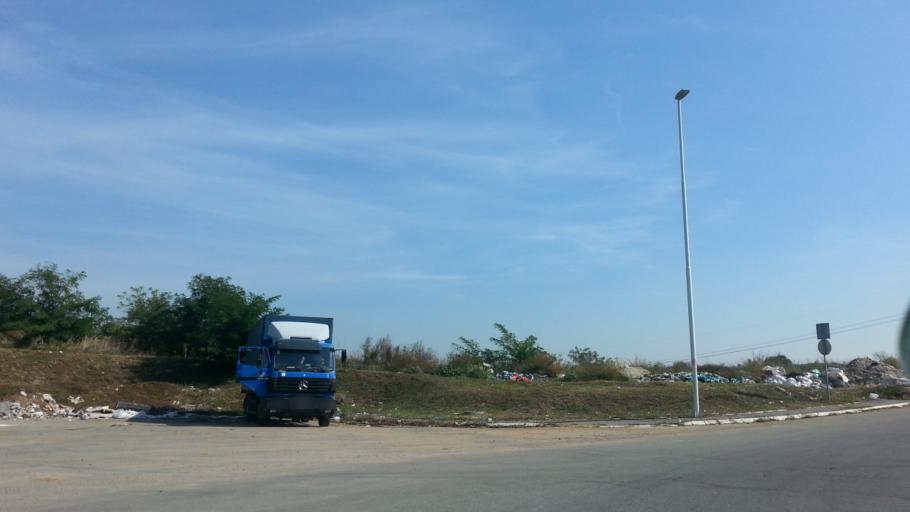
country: RS
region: Central Serbia
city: Sremcica
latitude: 44.7027
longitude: 20.4138
